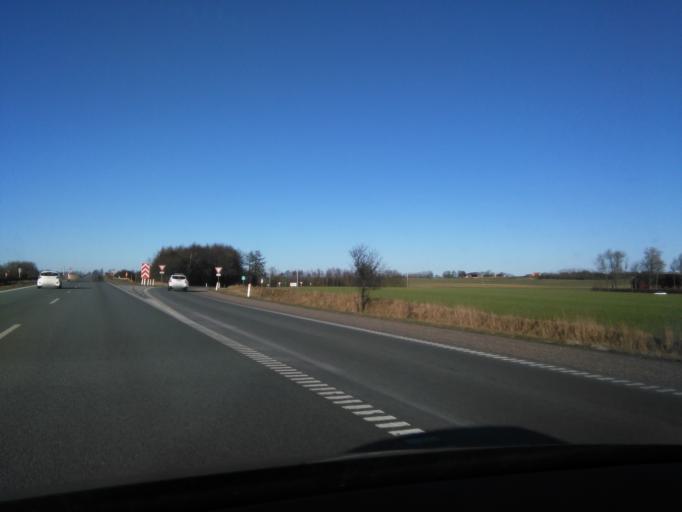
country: DK
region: Central Jutland
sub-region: Randers Kommune
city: Randers
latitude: 56.4885
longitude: 9.9805
